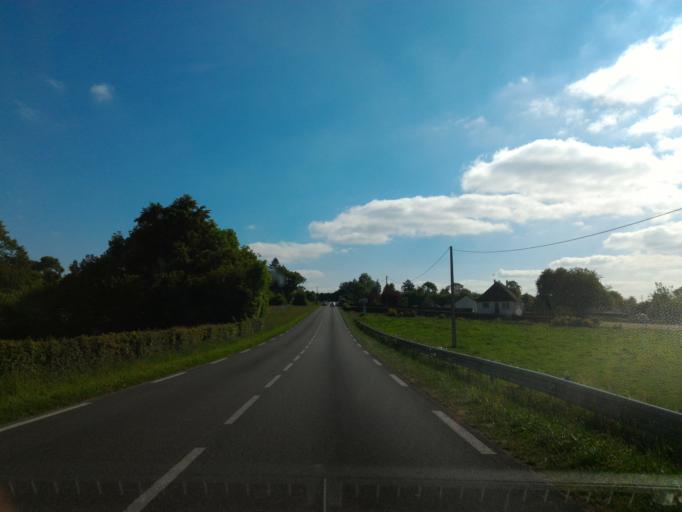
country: FR
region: Lower Normandy
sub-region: Departement de la Manche
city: Villedieu-les-Poeles
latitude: 48.8641
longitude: -1.2039
